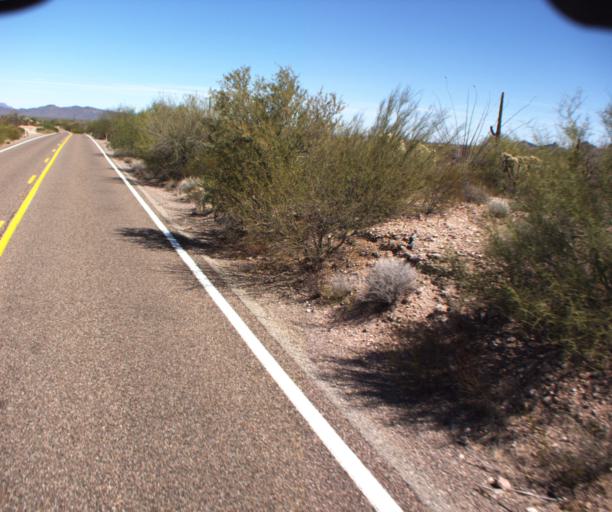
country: MX
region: Sonora
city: Sonoyta
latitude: 32.0970
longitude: -112.7725
